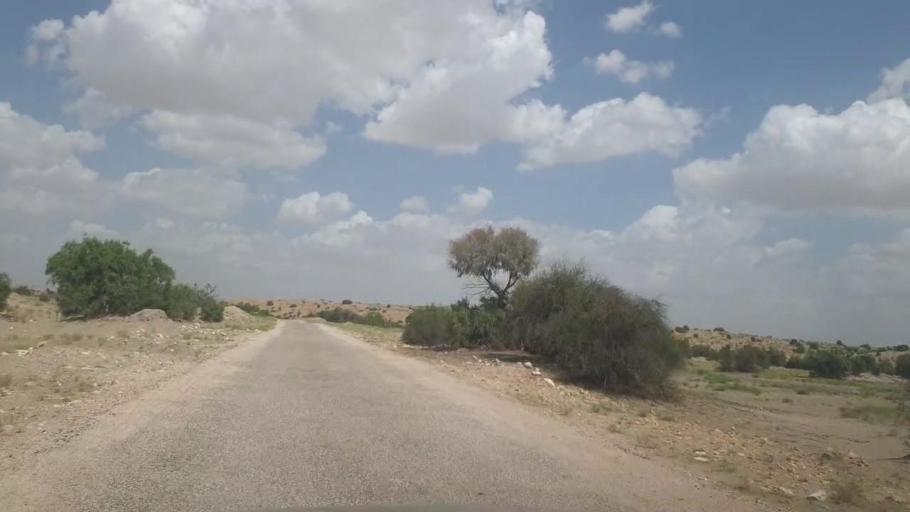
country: PK
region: Sindh
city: Kot Diji
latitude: 27.2534
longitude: 69.1551
